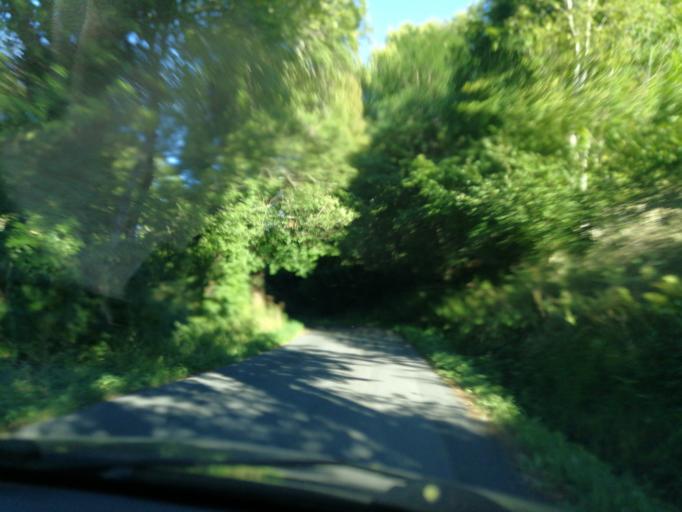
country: FR
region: Auvergne
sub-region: Departement du Cantal
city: Saint-Cernin
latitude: 45.0990
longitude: 2.5413
